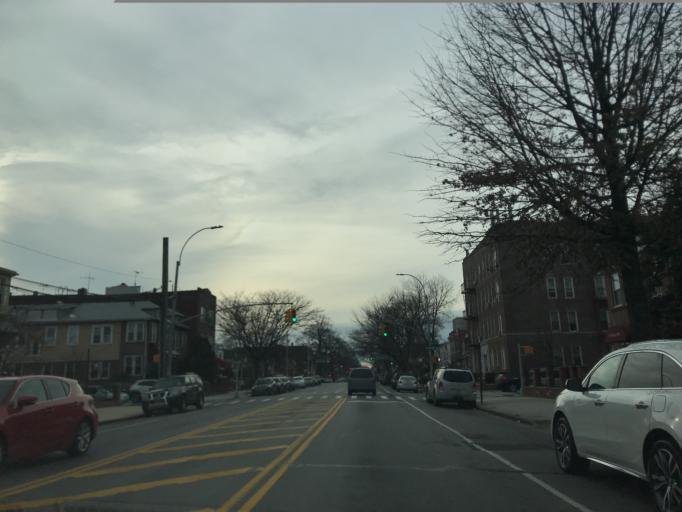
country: US
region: New York
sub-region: Kings County
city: Brooklyn
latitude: 40.6531
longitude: -73.9424
